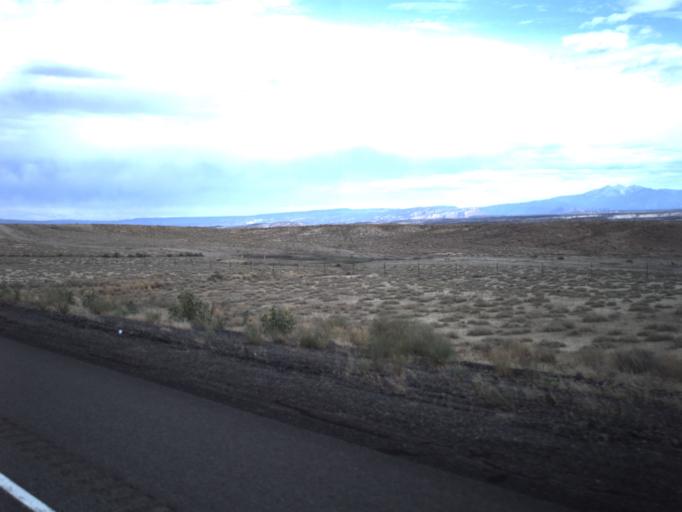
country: US
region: Utah
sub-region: Grand County
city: Moab
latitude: 38.9385
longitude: -109.4994
